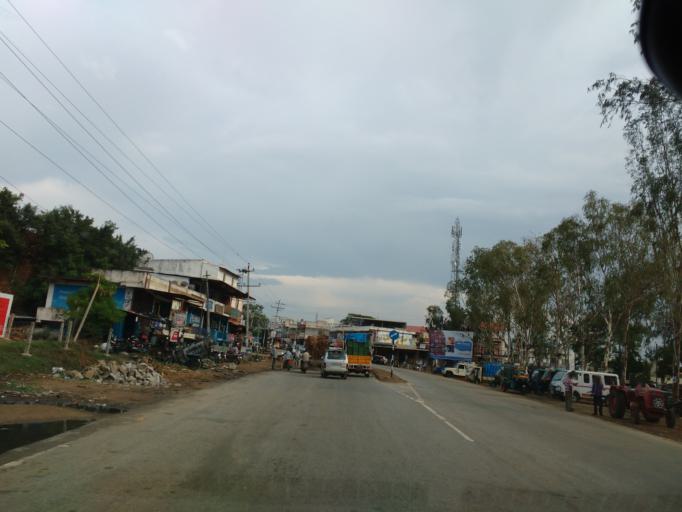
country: IN
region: Karnataka
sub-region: Hassan
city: Banavar
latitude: 13.4102
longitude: 76.1608
